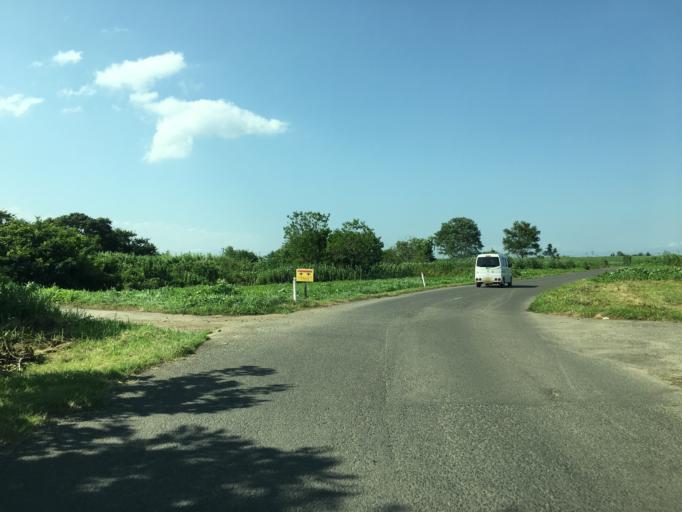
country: JP
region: Miyagi
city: Kakuda
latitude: 37.9648
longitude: 140.7883
